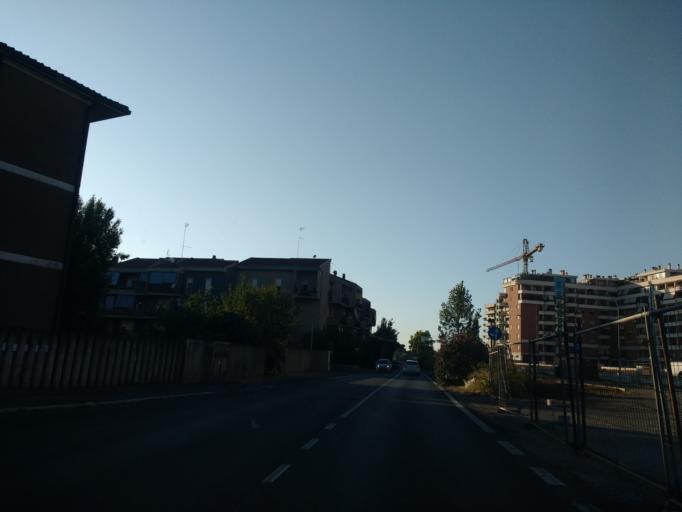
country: IT
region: Latium
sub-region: Citta metropolitana di Roma Capitale
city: Vitinia
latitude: 41.7707
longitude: 12.3735
